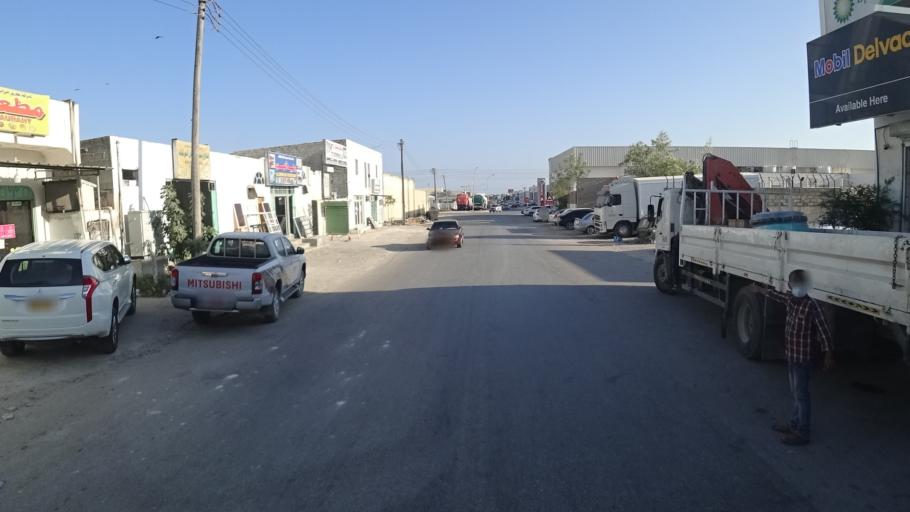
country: OM
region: Zufar
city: Salalah
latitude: 17.0190
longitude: 54.0437
